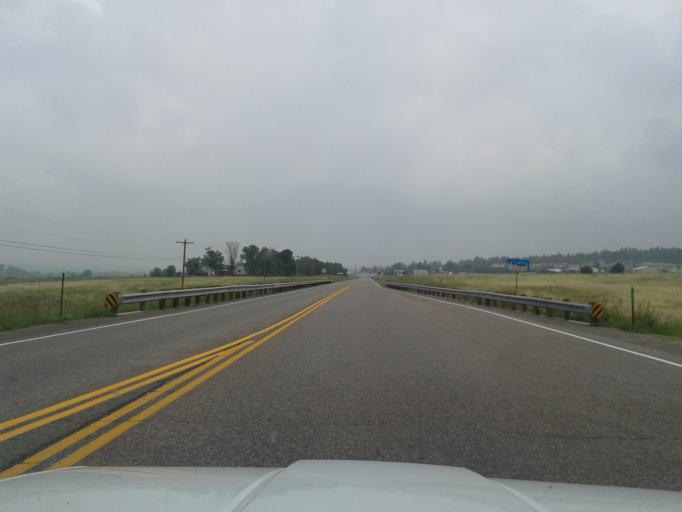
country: US
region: Colorado
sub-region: Douglas County
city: The Pinery
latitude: 39.3838
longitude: -104.7514
